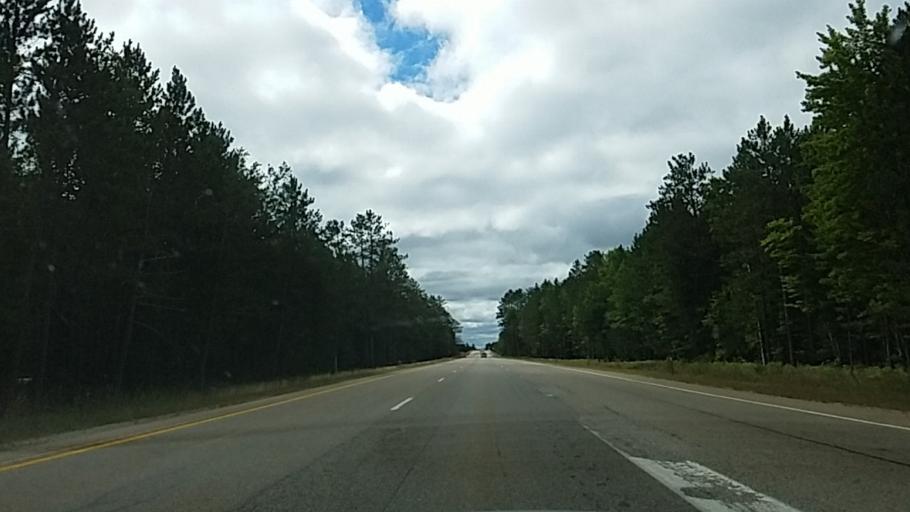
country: US
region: Michigan
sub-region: Crawford County
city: Grayling
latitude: 44.7107
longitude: -84.7000
